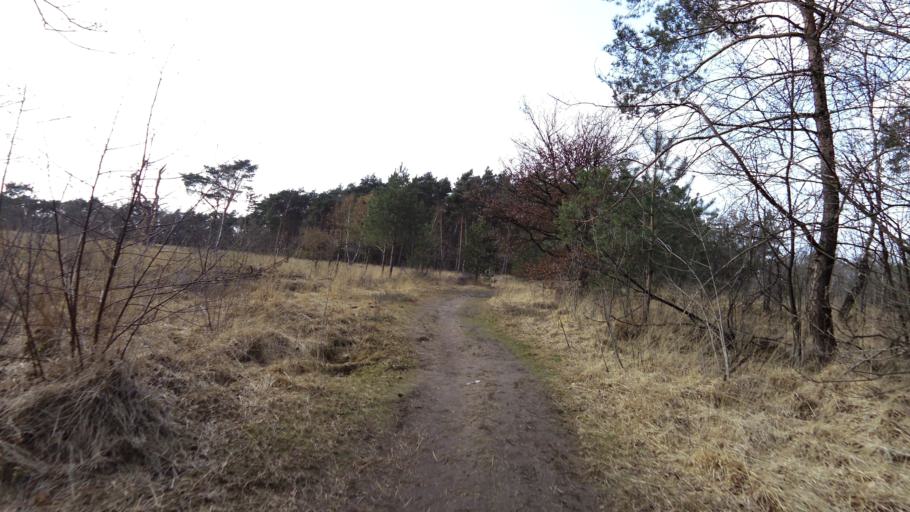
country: NL
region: Gelderland
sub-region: Gemeente Barneveld
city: Voorthuizen
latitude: 52.1930
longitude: 5.5735
